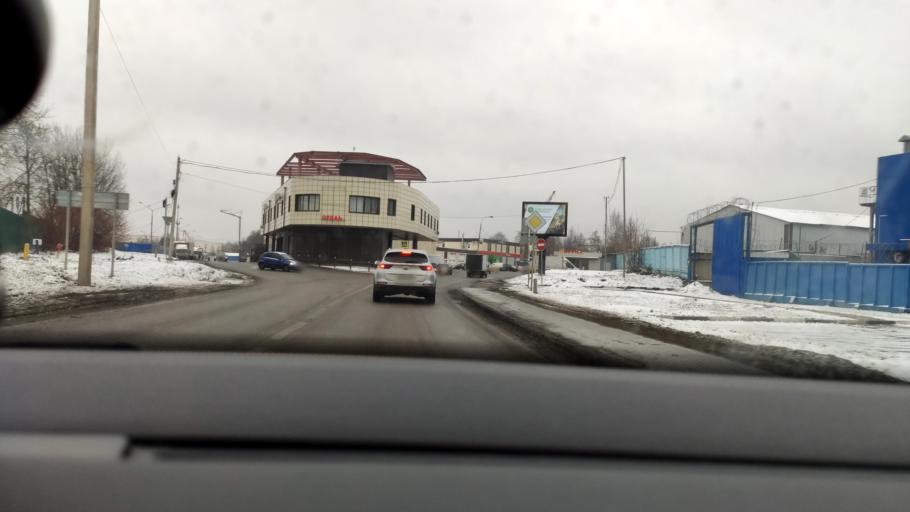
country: RU
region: Moscow
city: Khimki
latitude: 55.9199
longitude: 37.4205
